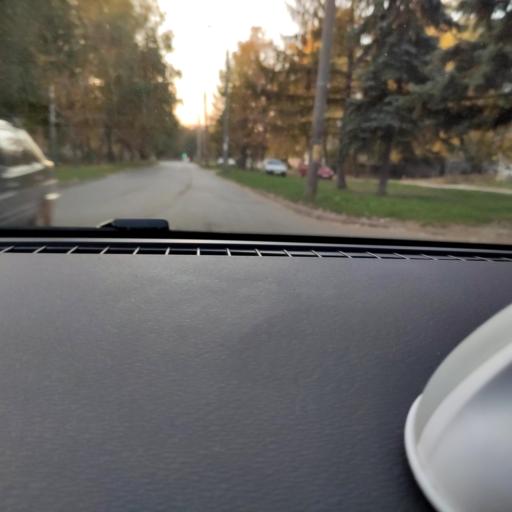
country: RU
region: Samara
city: Samara
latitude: 53.2182
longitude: 50.2271
